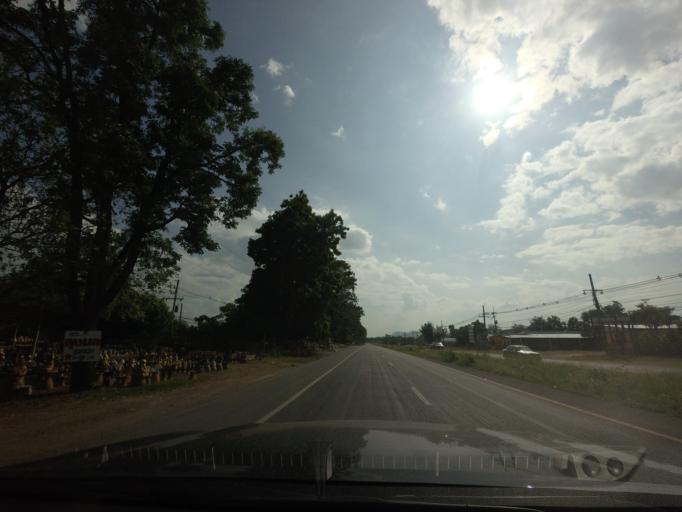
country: TH
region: Lop Buri
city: Chai Badan
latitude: 15.1846
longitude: 101.0749
